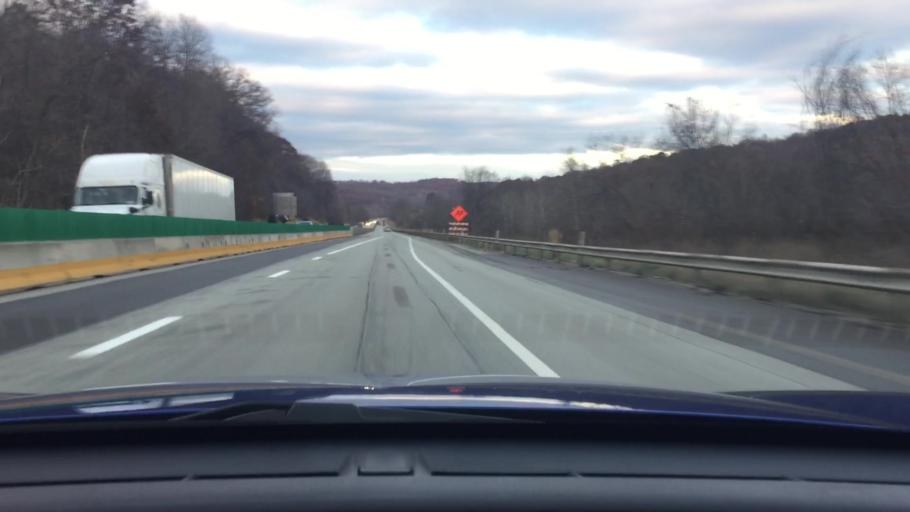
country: US
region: Pennsylvania
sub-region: Westmoreland County
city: New Stanton
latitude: 40.1962
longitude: -79.6850
